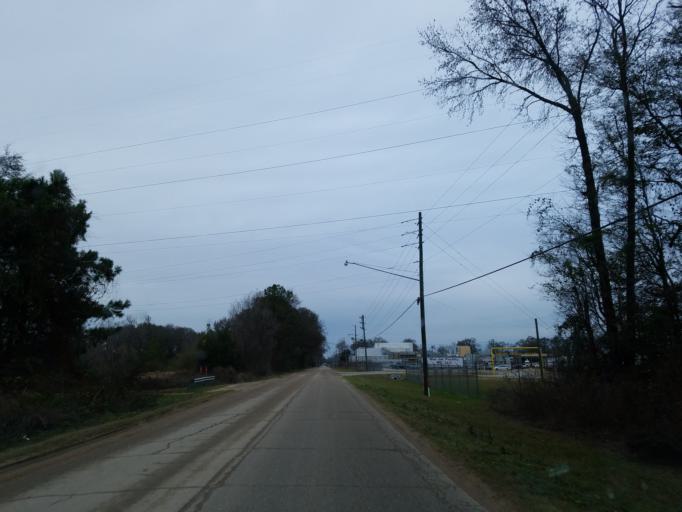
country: US
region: Mississippi
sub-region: Forrest County
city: Hattiesburg
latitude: 31.3028
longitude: -89.2768
